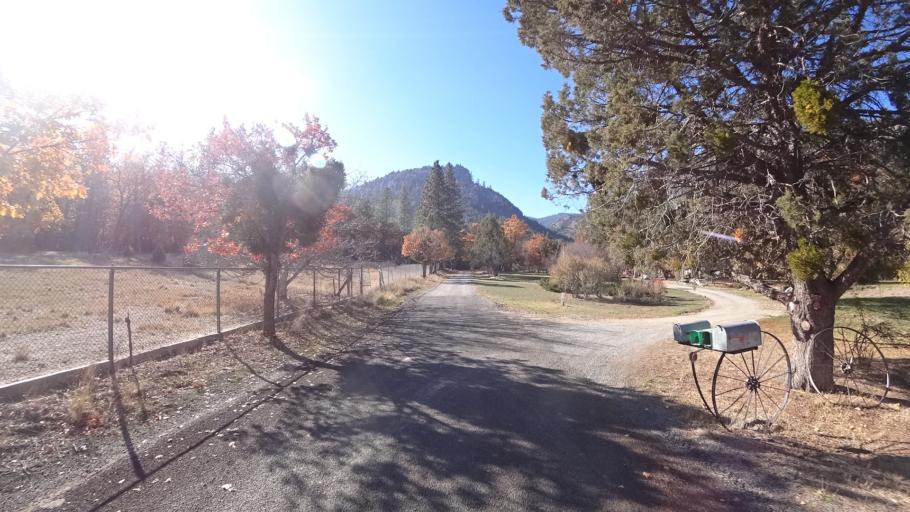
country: US
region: California
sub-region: Siskiyou County
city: Weed
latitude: 41.5029
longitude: -122.5913
